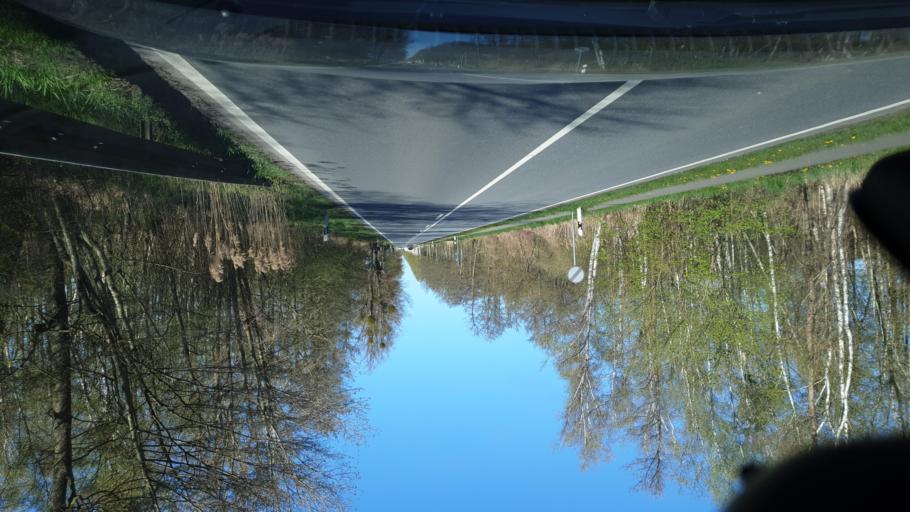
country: DE
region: Mecklenburg-Vorpommern
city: Werdervorstadt
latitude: 53.6631
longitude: 11.4494
